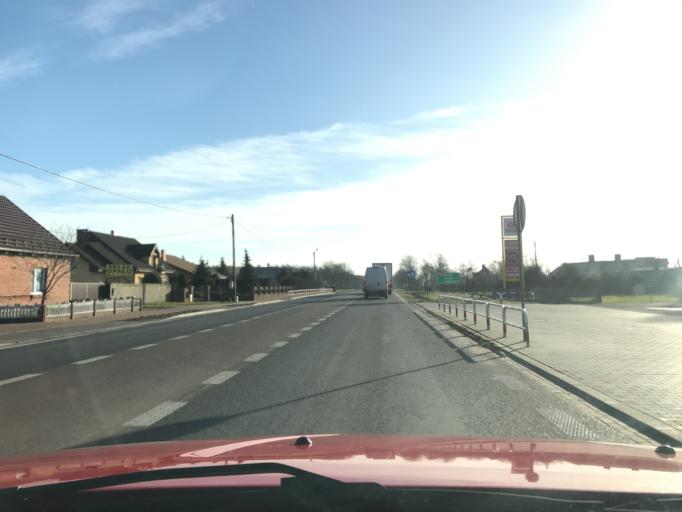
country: PL
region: Greater Poland Voivodeship
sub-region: Powiat pleszewski
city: Goluchow
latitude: 51.8651
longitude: 17.9022
